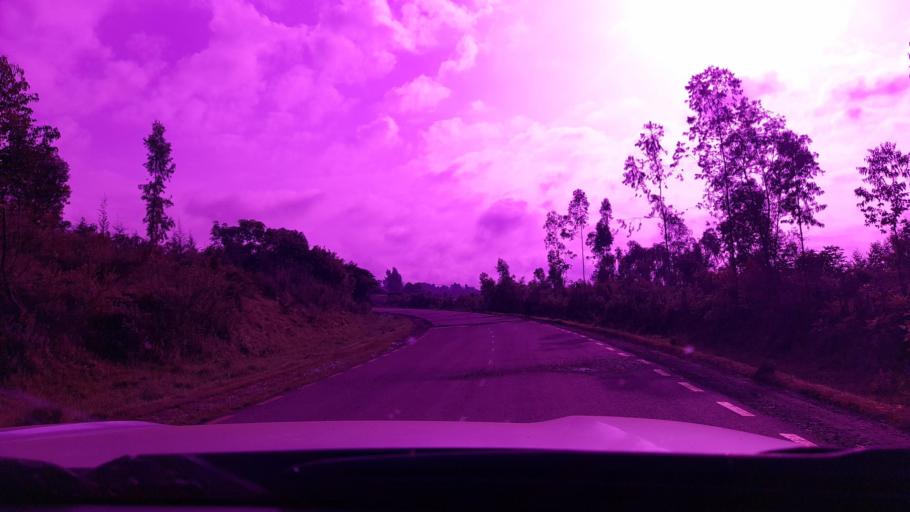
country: ET
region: Oromiya
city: Bedele
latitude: 8.2075
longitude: 36.4425
